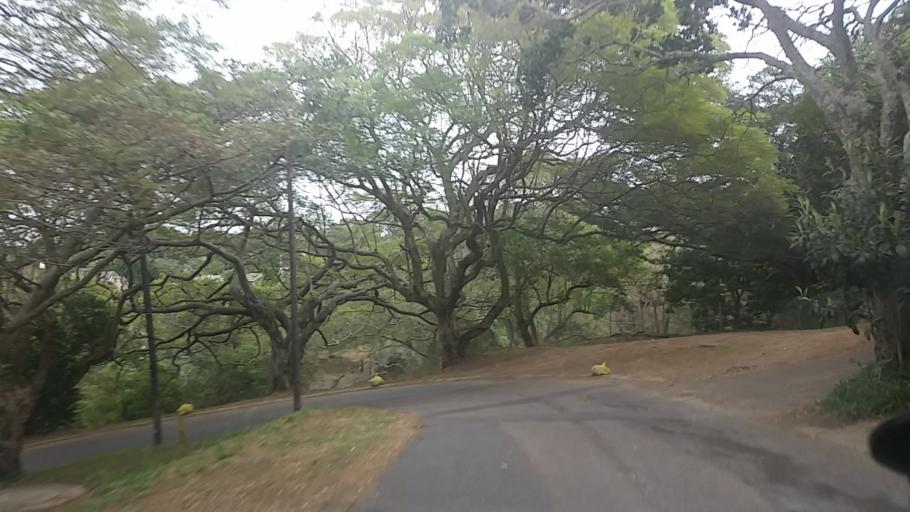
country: ZA
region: KwaZulu-Natal
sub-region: eThekwini Metropolitan Municipality
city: Berea
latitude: -29.8373
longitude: 30.9287
